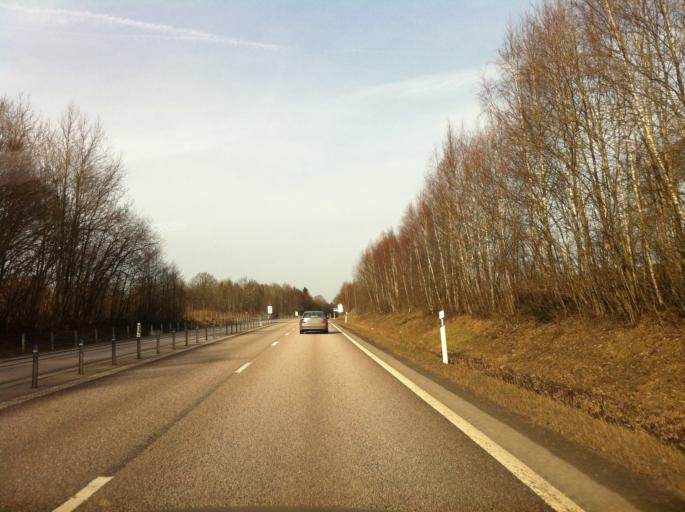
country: SE
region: Vaestra Goetaland
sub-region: Skovde Kommun
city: Stopen
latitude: 58.4578
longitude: 13.8478
